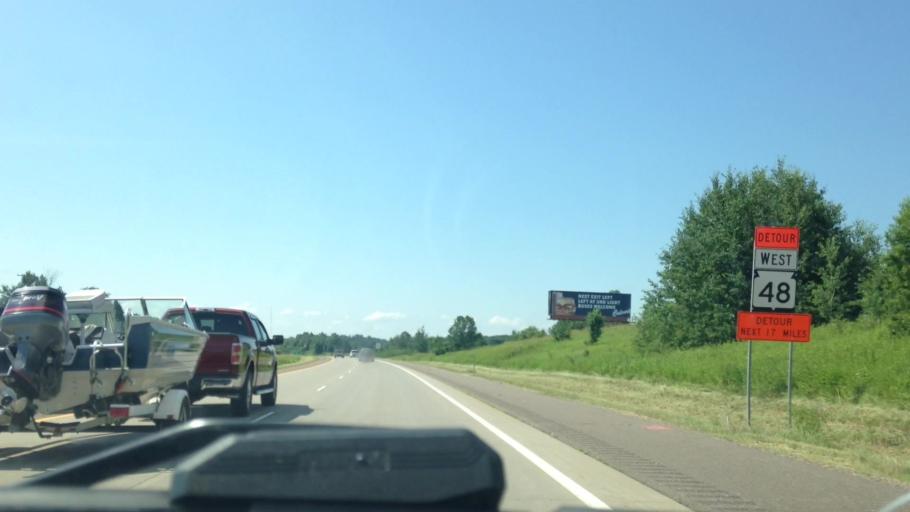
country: US
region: Wisconsin
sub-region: Barron County
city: Rice Lake
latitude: 45.5014
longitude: -91.7643
